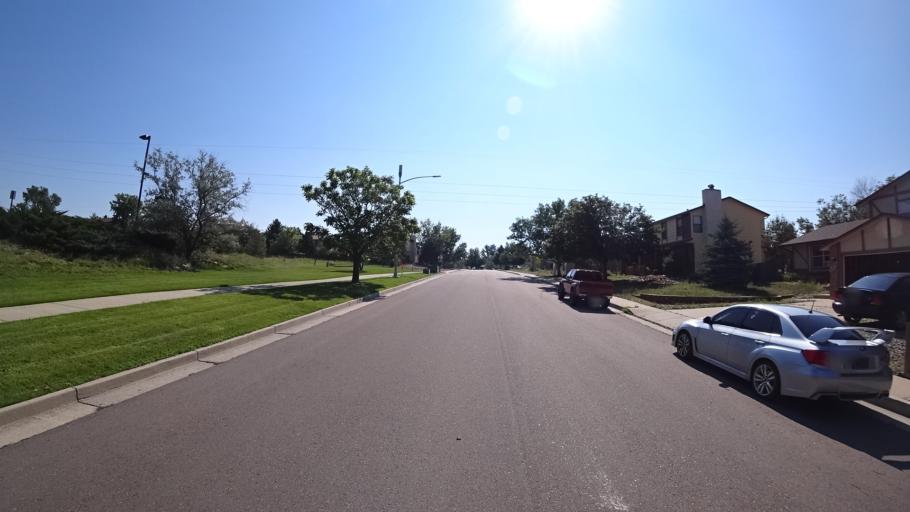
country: US
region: Colorado
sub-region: El Paso County
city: Air Force Academy
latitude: 38.9567
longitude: -104.7851
